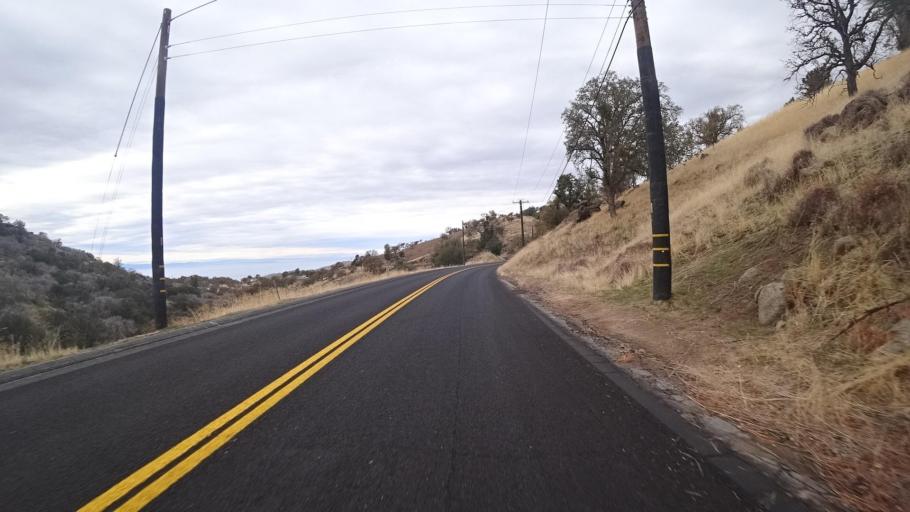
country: US
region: California
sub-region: Kern County
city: Stallion Springs
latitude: 35.0954
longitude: -118.6645
